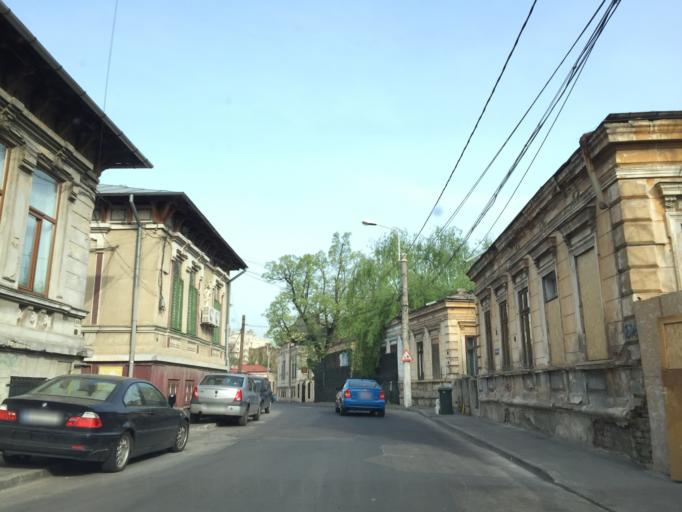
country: RO
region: Bucuresti
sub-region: Municipiul Bucuresti
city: Bucharest
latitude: 44.4276
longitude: 26.1151
